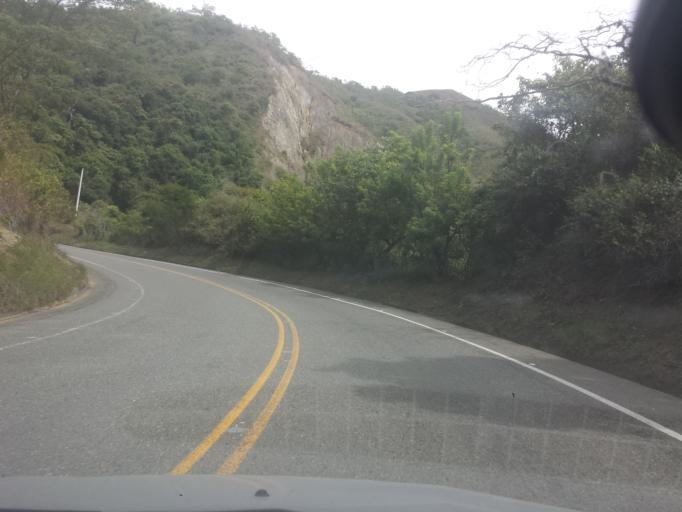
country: CO
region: Antioquia
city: Antioquia
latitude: 6.6201
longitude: -75.8734
